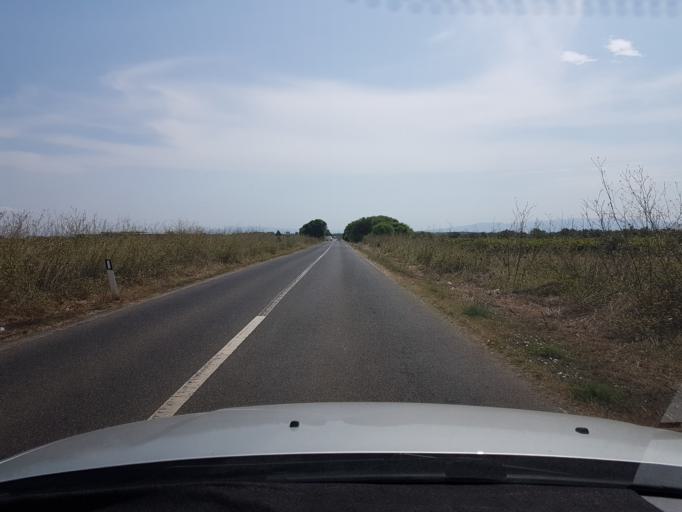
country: IT
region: Sardinia
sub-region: Provincia di Oristano
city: Cabras
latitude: 39.9166
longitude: 8.4760
